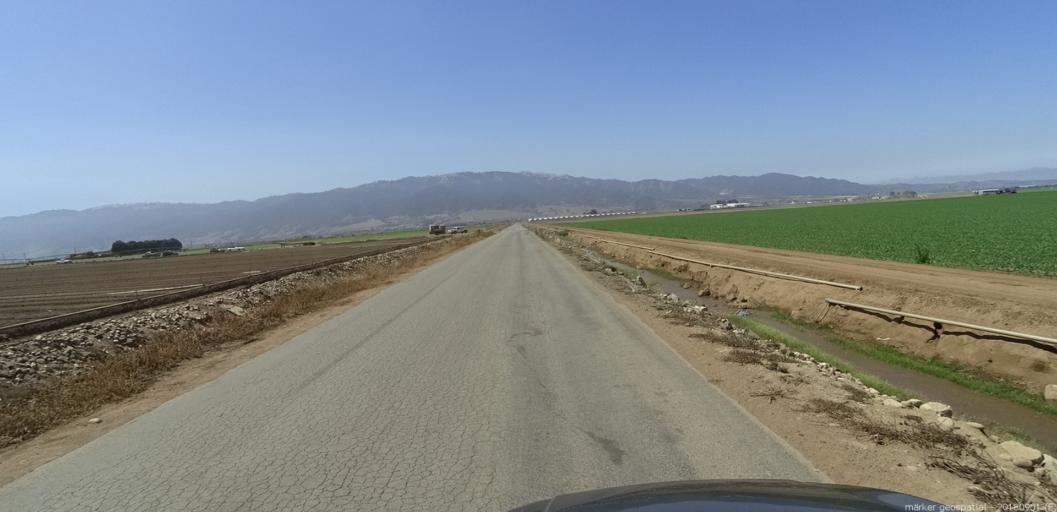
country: US
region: California
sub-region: Monterey County
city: Chualar
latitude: 36.5982
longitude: -121.5232
